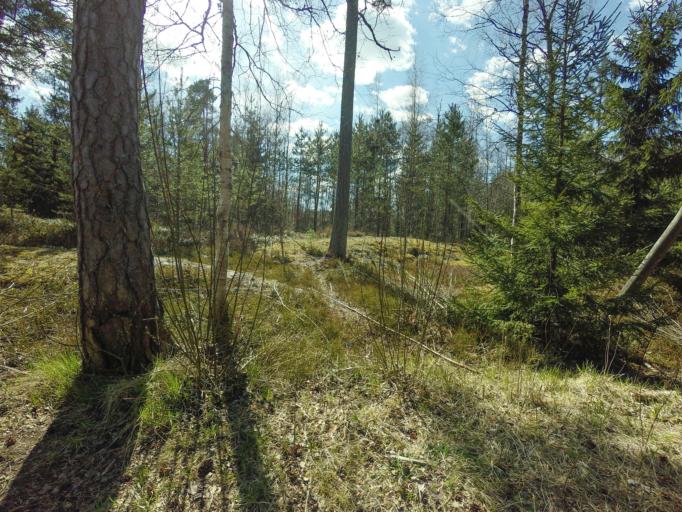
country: FI
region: Uusimaa
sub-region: Helsinki
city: Helsinki
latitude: 60.1644
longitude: 25.0382
